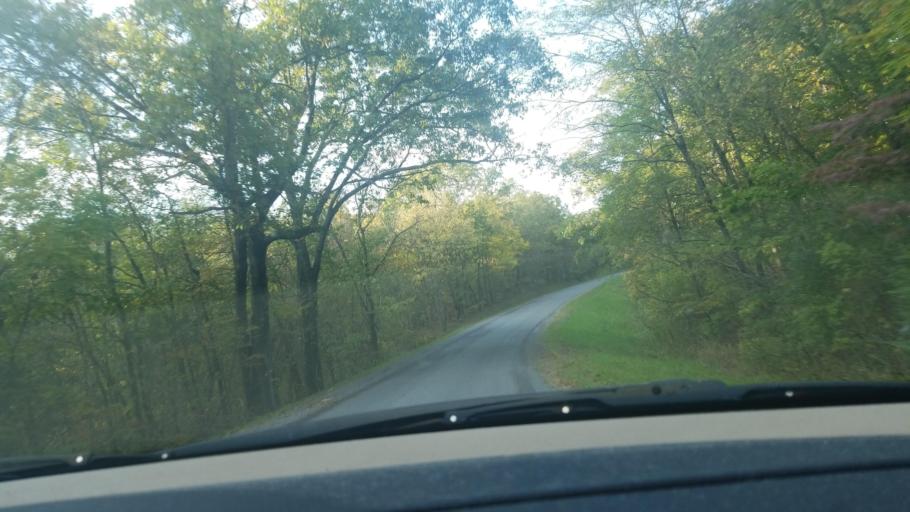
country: US
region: Illinois
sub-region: Saline County
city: Carrier Mills
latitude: 37.7748
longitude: -88.7148
